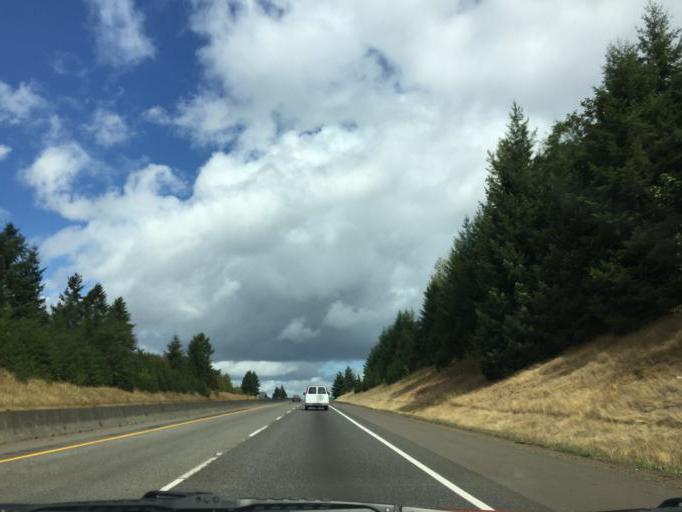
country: US
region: Washington
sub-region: Lewis County
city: Winlock
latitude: 46.4471
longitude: -122.8874
